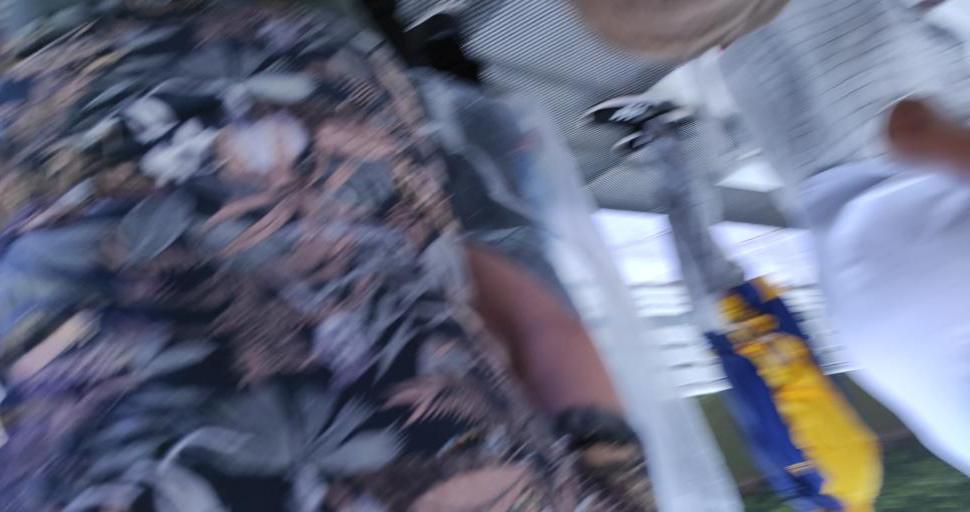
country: AR
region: Misiones
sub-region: Departamento de Iguazu
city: Puerto Iguazu
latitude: -25.5881
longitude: -54.5559
